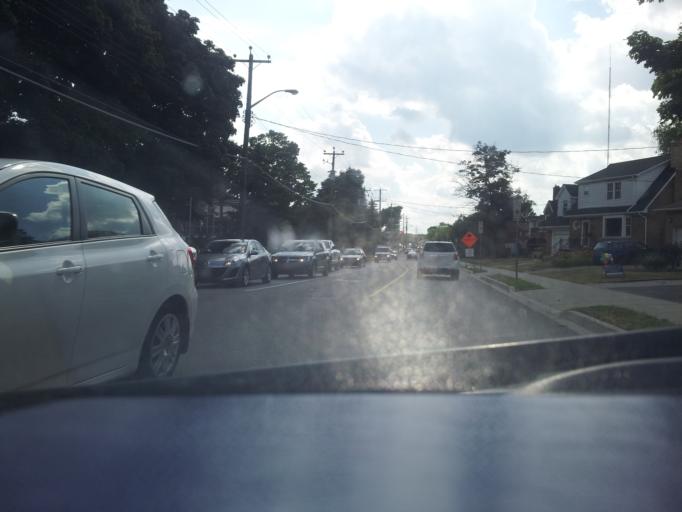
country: CA
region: Ontario
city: Kitchener
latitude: 43.4412
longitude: -80.5025
